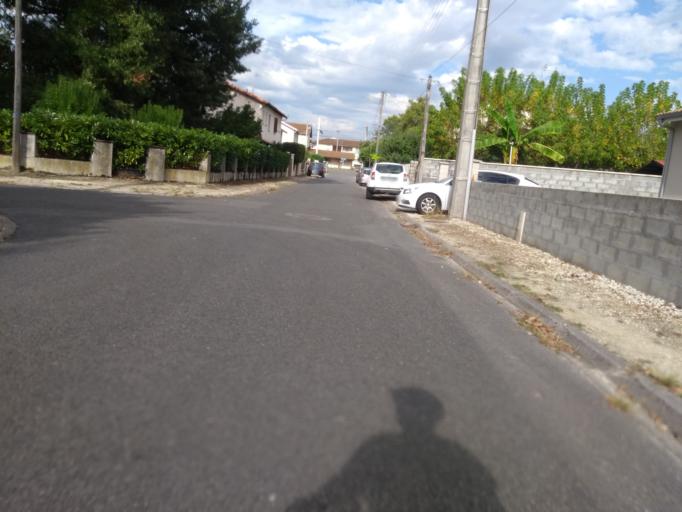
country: FR
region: Aquitaine
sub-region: Departement de la Gironde
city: Saint-Aubin-de-Medoc
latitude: 44.7713
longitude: -0.6983
